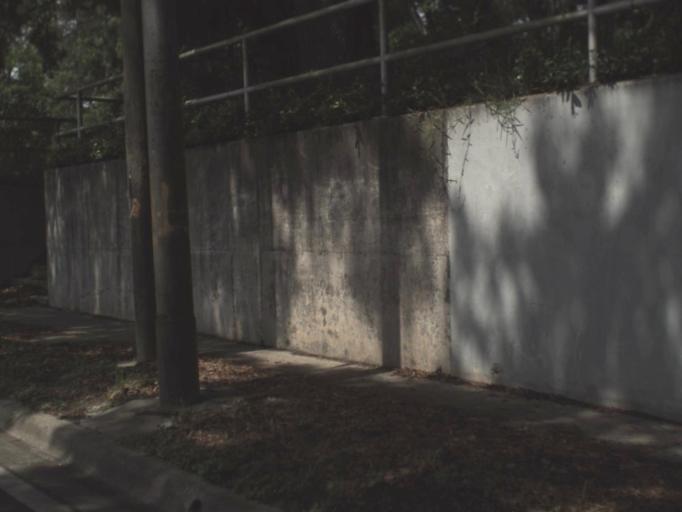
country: US
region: Florida
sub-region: Duval County
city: Jacksonville
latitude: 30.3153
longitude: -81.5993
